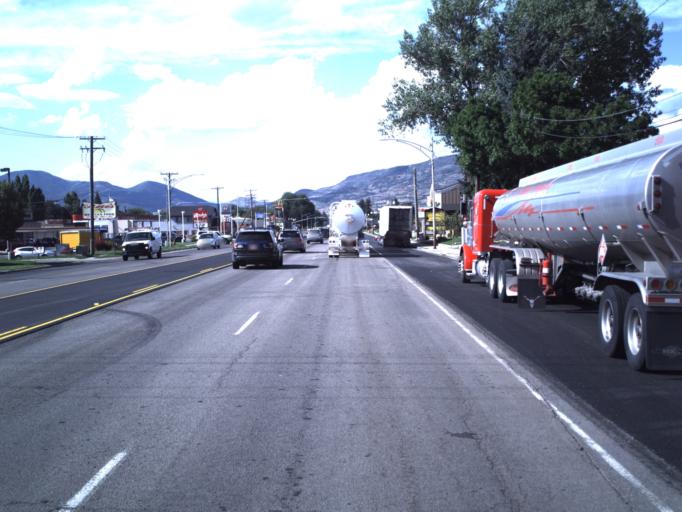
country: US
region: Utah
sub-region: Wasatch County
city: Heber
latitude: 40.4963
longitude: -111.4135
